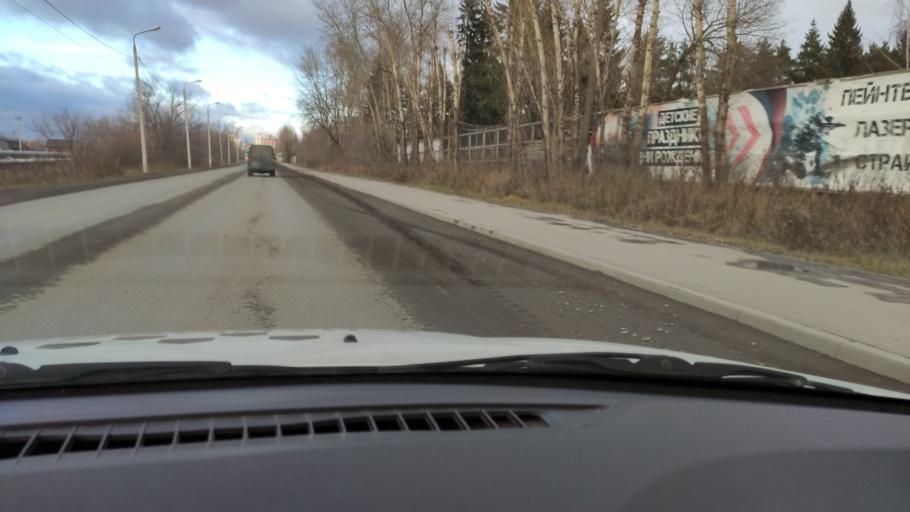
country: RU
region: Perm
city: Kondratovo
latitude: 57.9747
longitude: 56.1289
